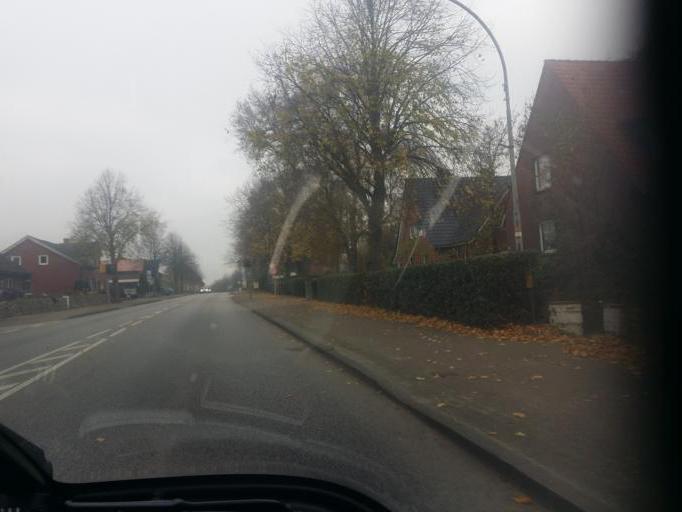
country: DE
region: Schleswig-Holstein
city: Hattstedt
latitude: 54.5237
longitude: 9.0283
